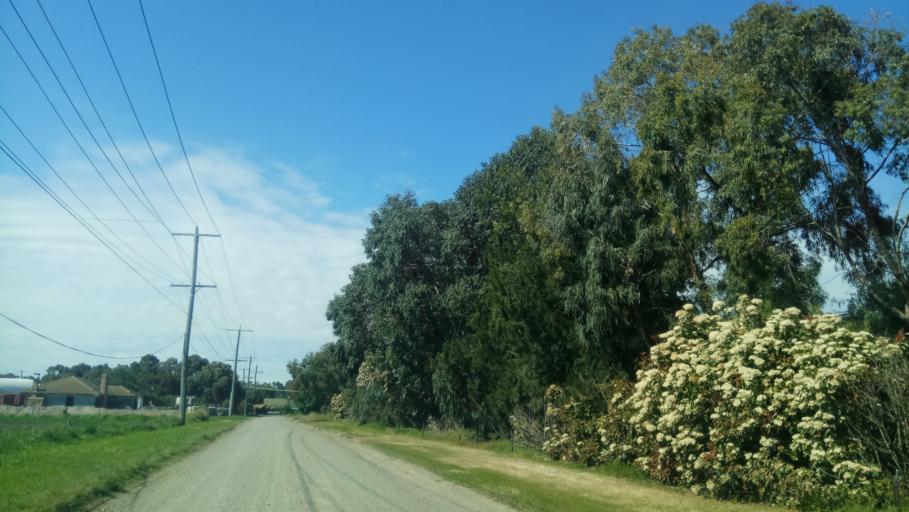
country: AU
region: Victoria
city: Heatherton
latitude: -37.9599
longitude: 145.0979
